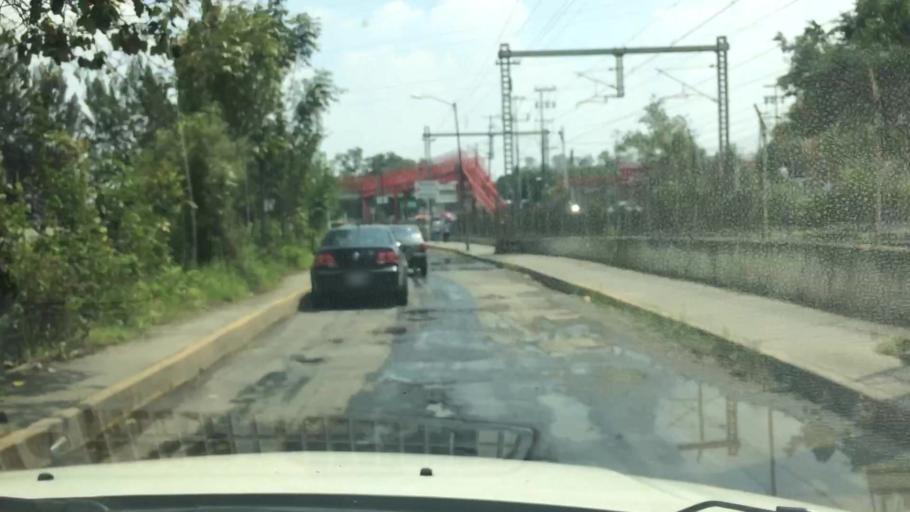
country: MX
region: Mexico City
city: Xochimilco
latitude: 19.2695
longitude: -99.1283
